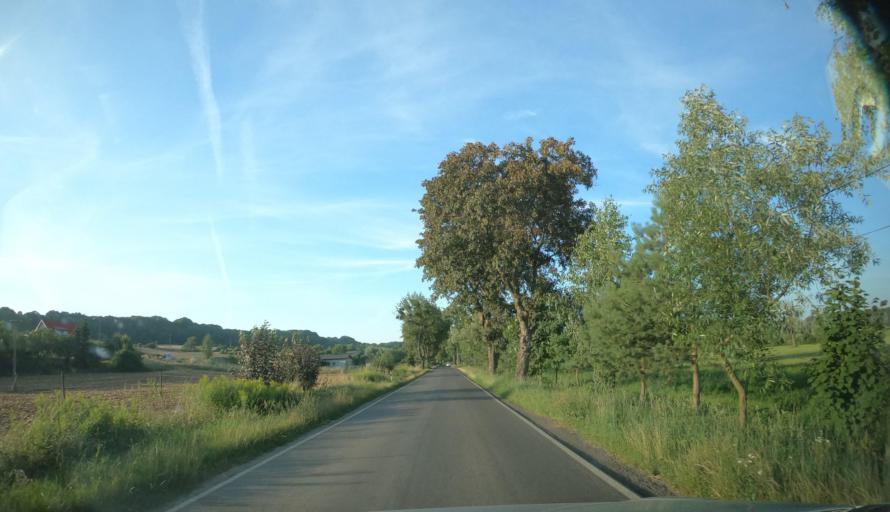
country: PL
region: Kujawsko-Pomorskie
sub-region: Bydgoszcz
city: Fordon
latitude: 53.2104
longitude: 18.1792
